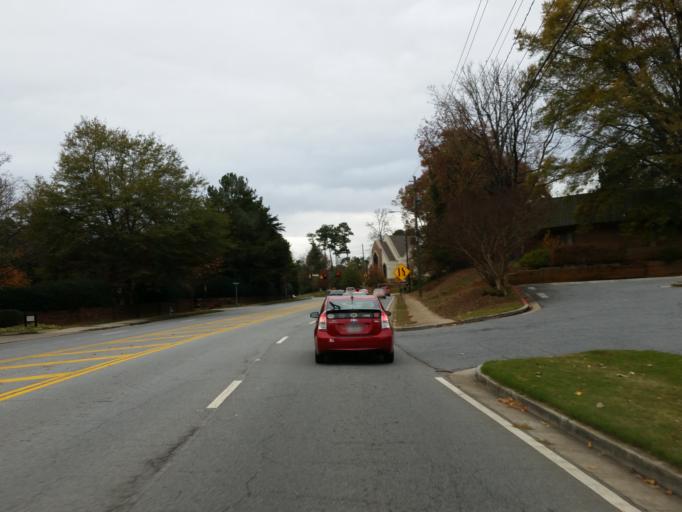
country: US
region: Georgia
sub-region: Fulton County
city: Sandy Springs
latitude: 33.9174
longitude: -84.3630
